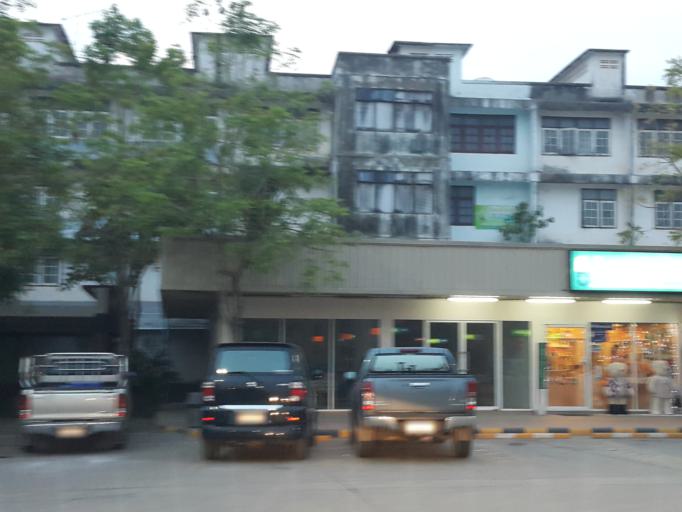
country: TH
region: Suphan Buri
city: Dan Chang
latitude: 14.8410
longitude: 99.6894
